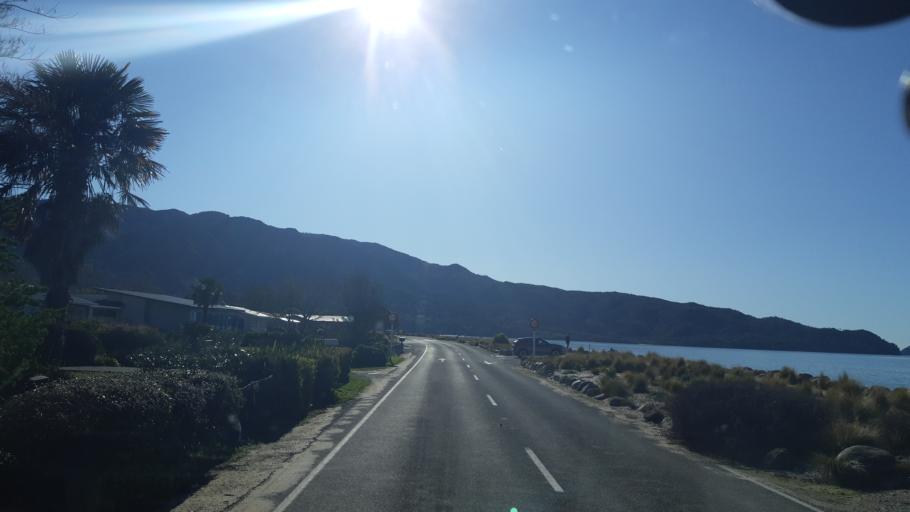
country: NZ
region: Tasman
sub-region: Tasman District
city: Motueka
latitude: -41.0066
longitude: 173.0094
